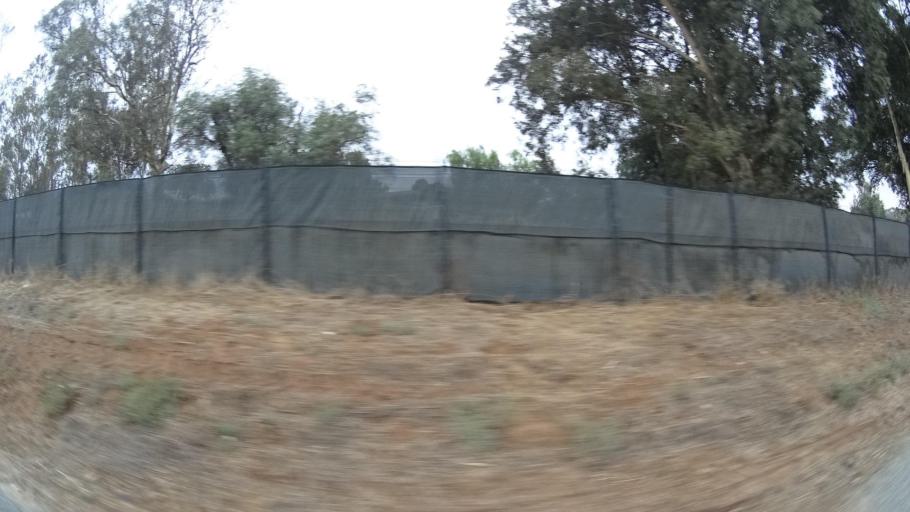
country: US
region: California
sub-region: San Diego County
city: San Pasqual
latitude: 33.0917
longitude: -116.9949
